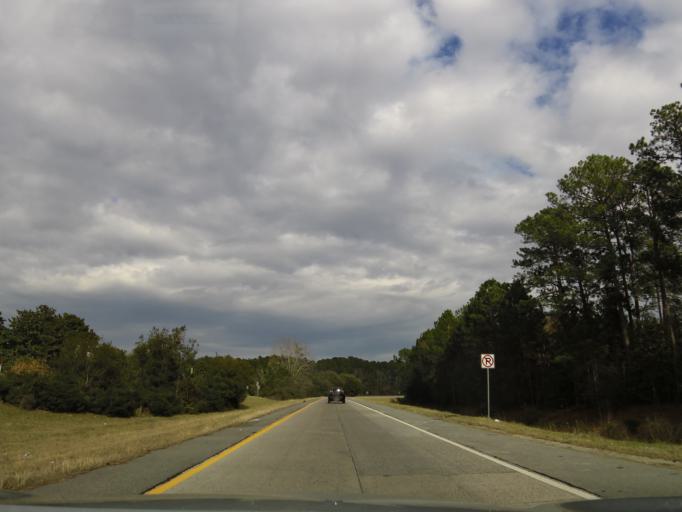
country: US
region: Georgia
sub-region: Chatham County
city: Pooler
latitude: 32.0721
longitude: -81.2455
